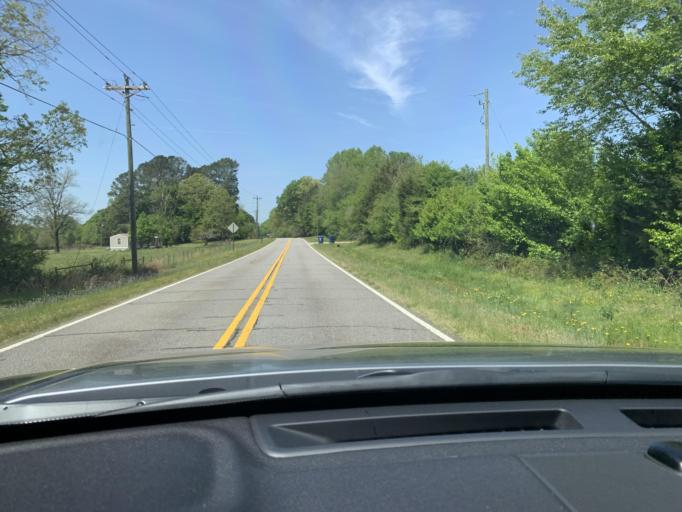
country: US
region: Georgia
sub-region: Barrow County
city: Statham
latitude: 33.9004
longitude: -83.6057
